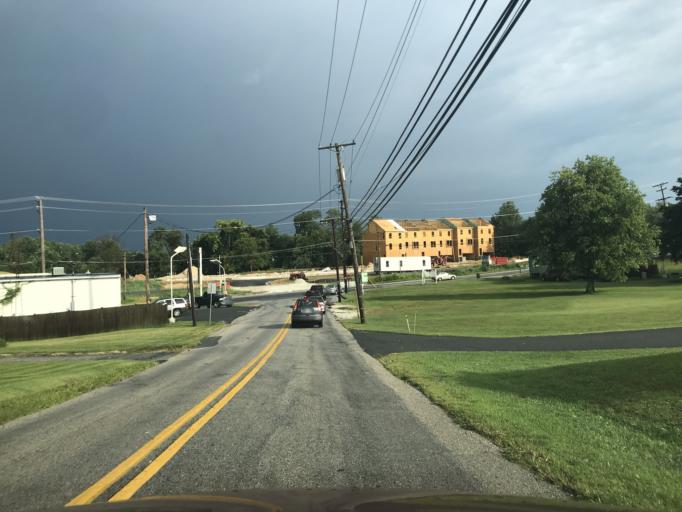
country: US
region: Maryland
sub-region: Baltimore County
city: Carney
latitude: 39.4110
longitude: -76.5133
